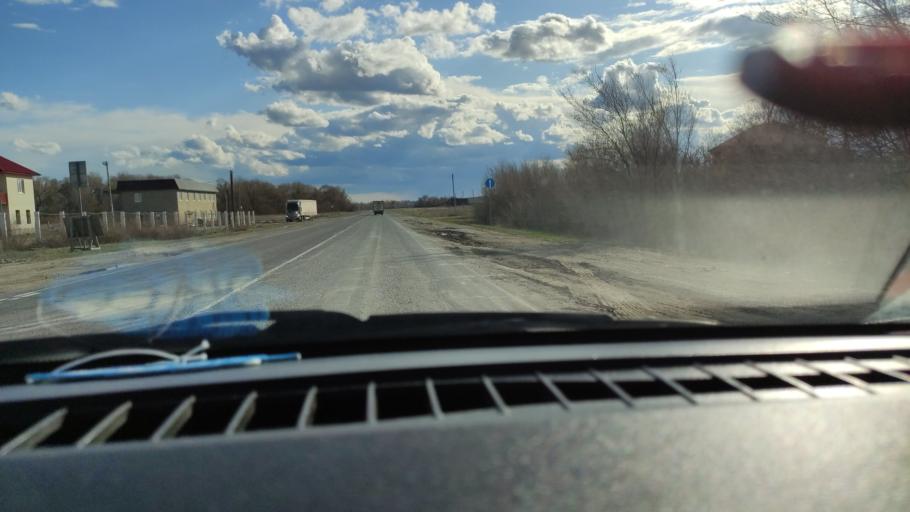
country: RU
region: Saratov
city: Sinodskoye
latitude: 52.0441
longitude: 46.7402
